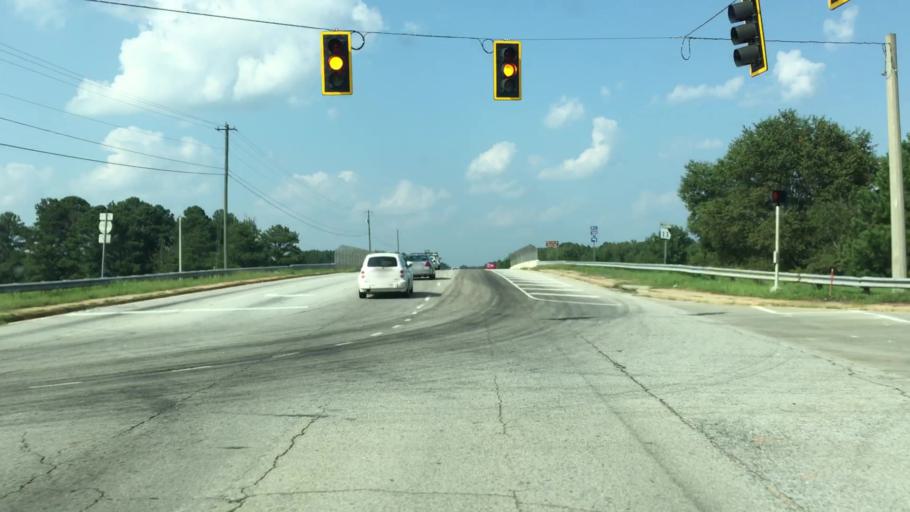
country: US
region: Georgia
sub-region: Walton County
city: Social Circle
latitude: 33.6113
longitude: -83.7506
